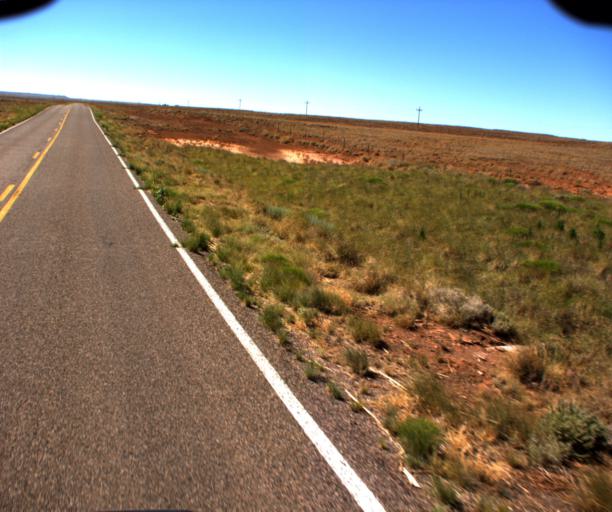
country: US
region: Arizona
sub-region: Coconino County
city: LeChee
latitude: 35.1861
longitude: -110.9338
